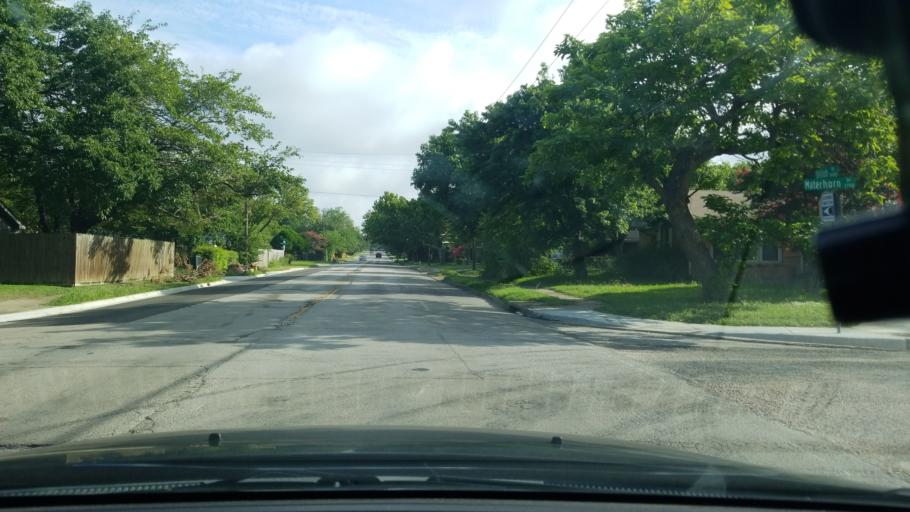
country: US
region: Texas
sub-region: Dallas County
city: Garland
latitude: 32.8285
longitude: -96.6681
